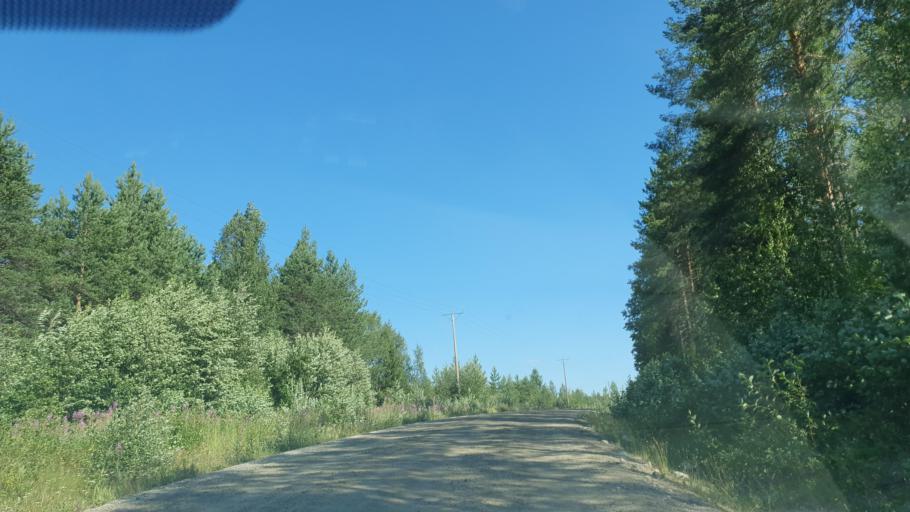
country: FI
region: Kainuu
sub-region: Kehys-Kainuu
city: Kuhmo
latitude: 64.0497
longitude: 29.6136
